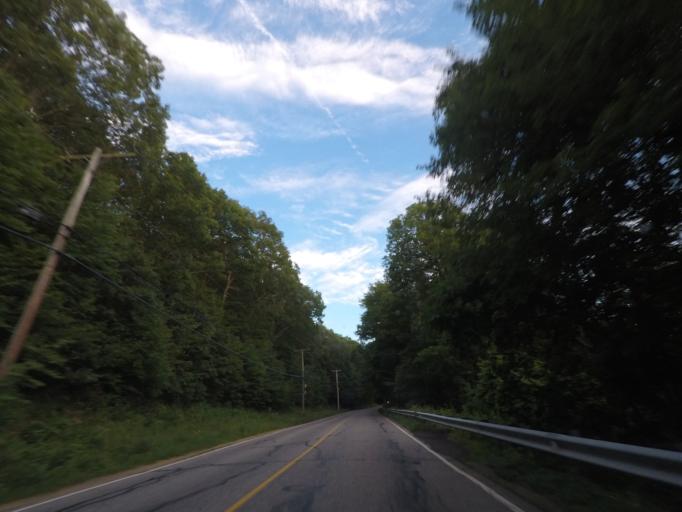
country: US
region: Massachusetts
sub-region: Worcester County
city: Warren
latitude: 42.1966
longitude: -72.1807
